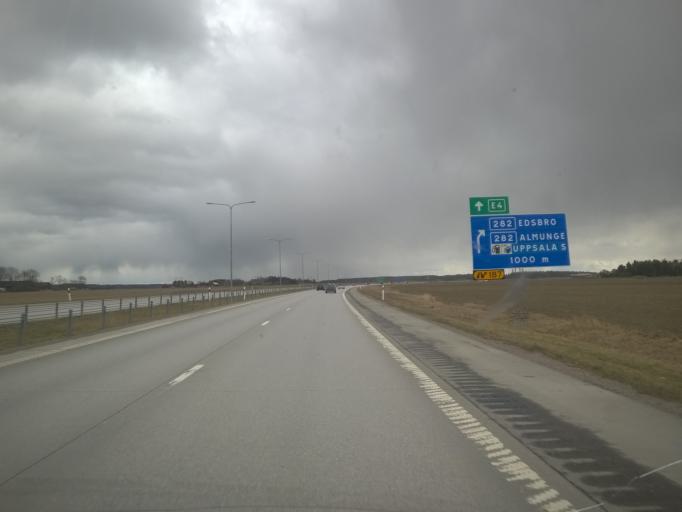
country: SE
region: Uppsala
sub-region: Uppsala Kommun
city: Saevja
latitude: 59.8603
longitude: 17.7255
